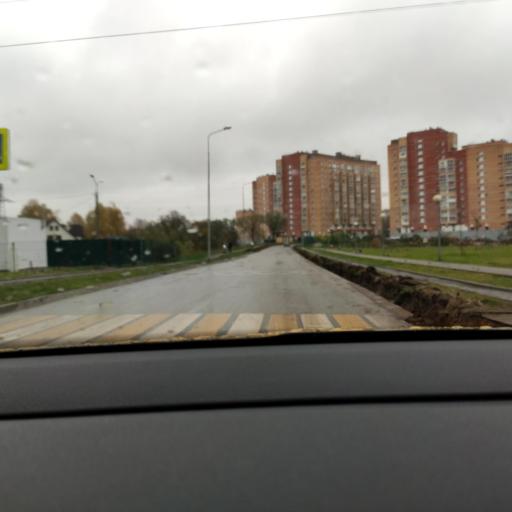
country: RU
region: Moskovskaya
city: Shcherbinka
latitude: 55.5022
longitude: 37.5384
